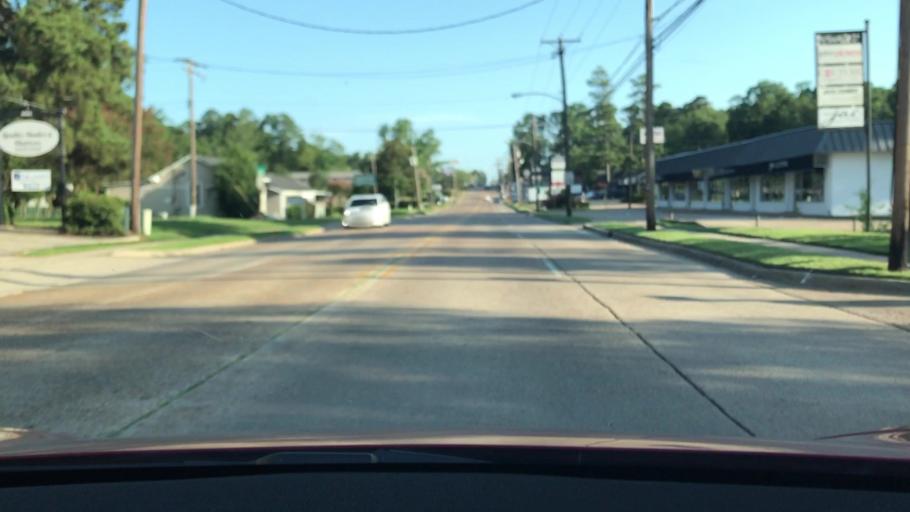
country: US
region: Louisiana
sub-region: Bossier Parish
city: Bossier City
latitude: 32.4530
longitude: -93.7461
